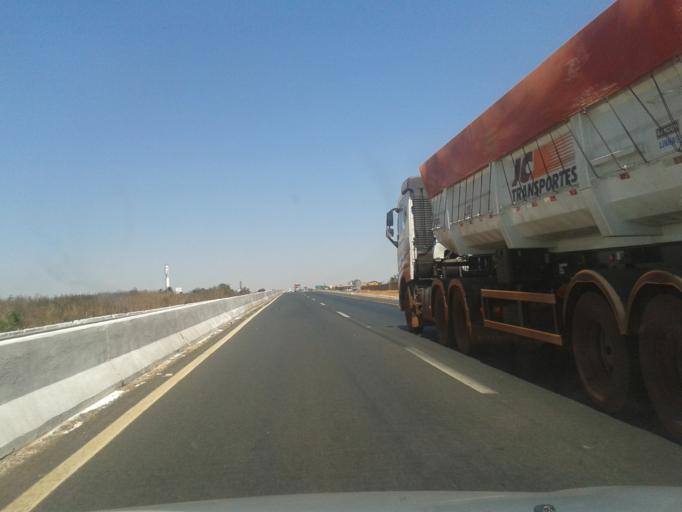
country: BR
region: Minas Gerais
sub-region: Uberlandia
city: Uberlandia
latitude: -18.9203
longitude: -48.2224
